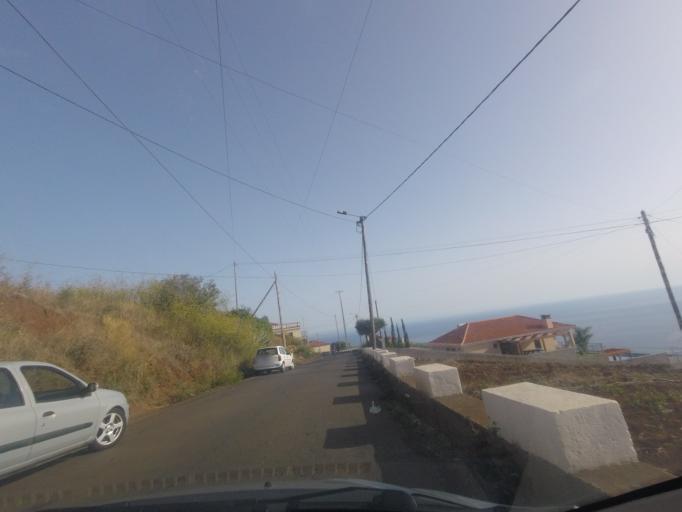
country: PT
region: Madeira
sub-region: Calheta
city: Arco da Calheta
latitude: 32.7034
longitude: -17.1257
